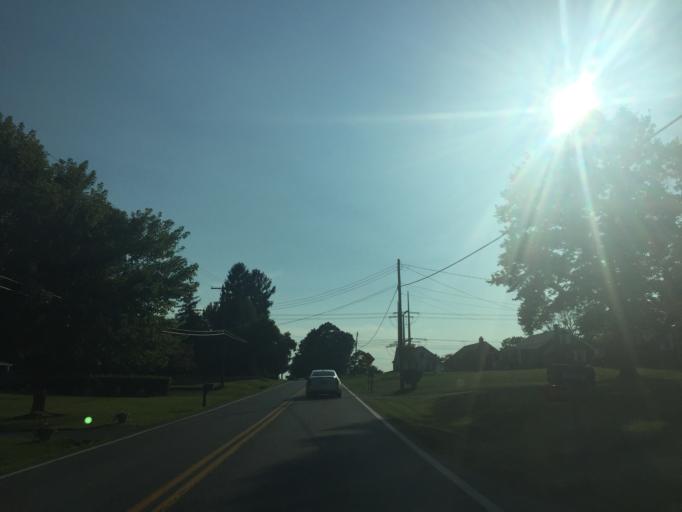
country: US
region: Maryland
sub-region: Montgomery County
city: Damascus
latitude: 39.3376
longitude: -77.2097
